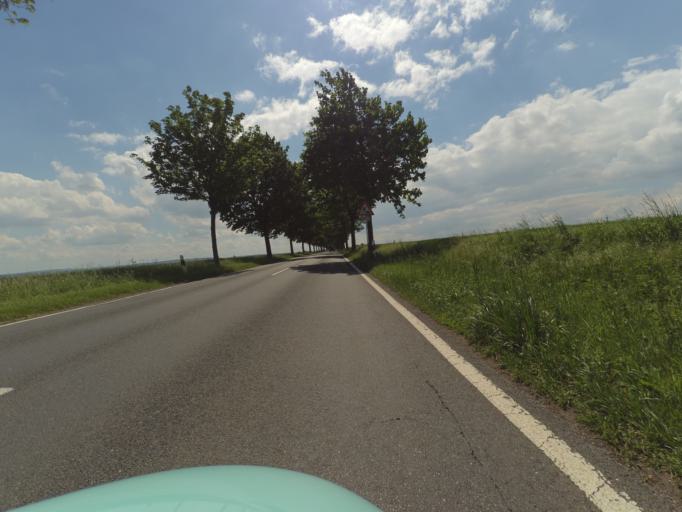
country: DE
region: Lower Saxony
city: Hohenhameln
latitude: 52.2113
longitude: 10.0368
